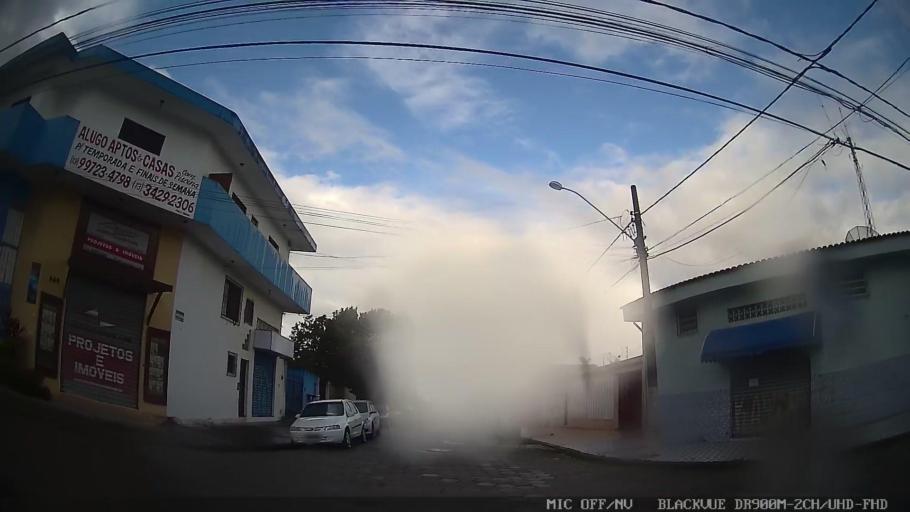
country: BR
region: Sao Paulo
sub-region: Itanhaem
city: Itanhaem
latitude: -24.2390
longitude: -46.8965
